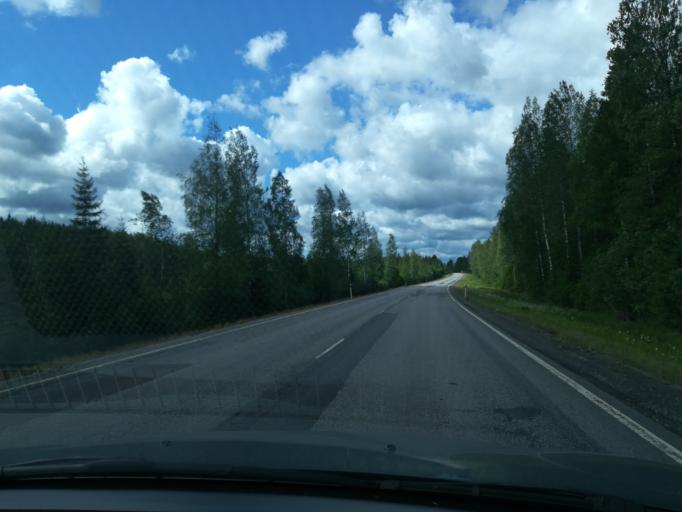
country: FI
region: Southern Savonia
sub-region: Mikkeli
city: Ristiina
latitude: 61.4329
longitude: 27.2398
